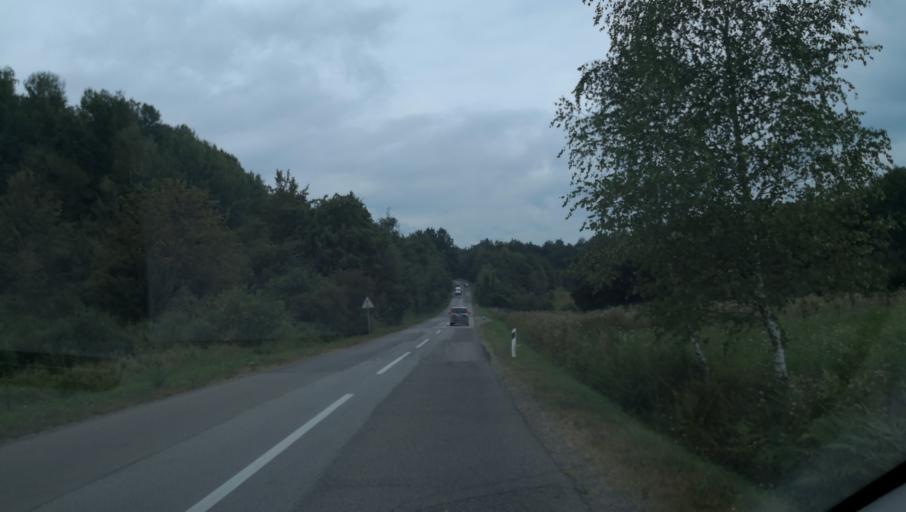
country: HR
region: Karlovacka
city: Ozalj
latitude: 45.5185
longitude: 15.3941
